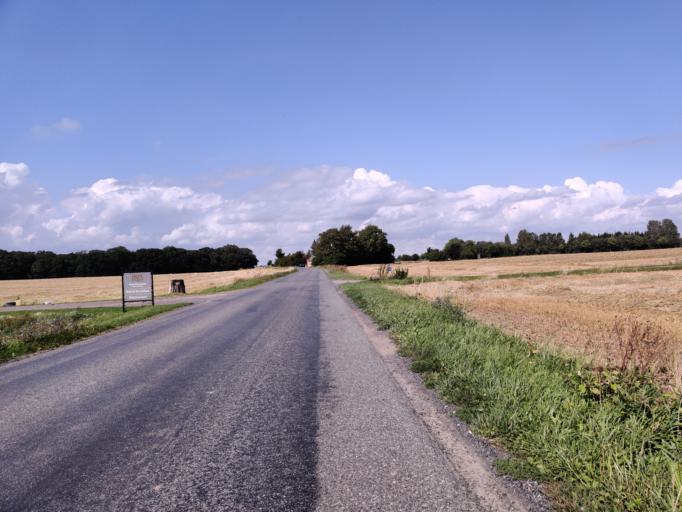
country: DK
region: Zealand
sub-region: Guldborgsund Kommune
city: Nykobing Falster
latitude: 54.6394
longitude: 11.8973
